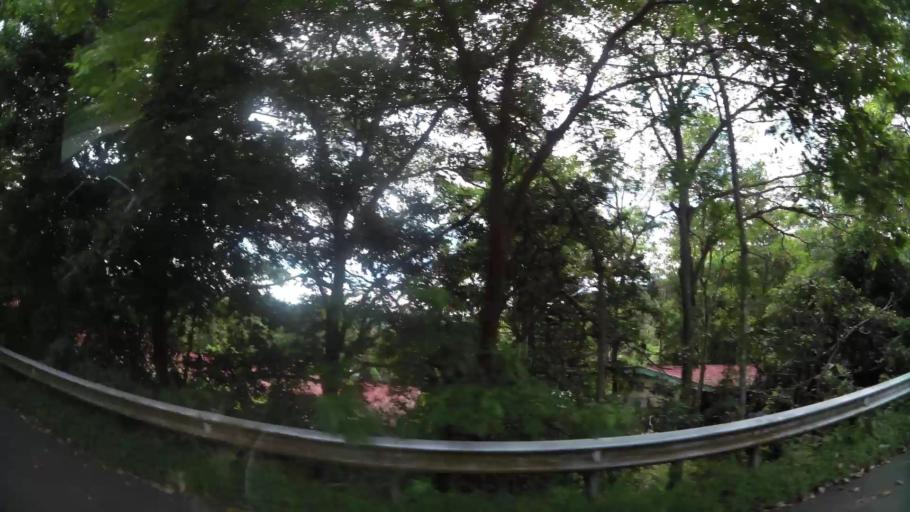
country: PA
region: Panama
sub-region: Distrito de Panama
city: Paraiso
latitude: 9.0349
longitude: -79.6270
